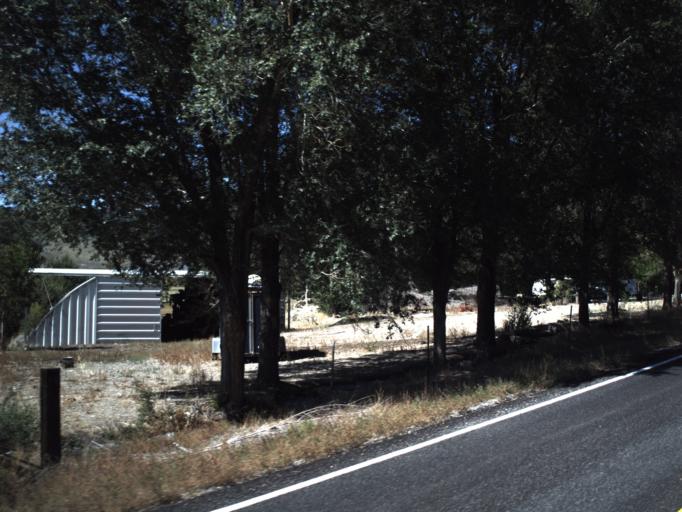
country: US
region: Utah
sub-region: Piute County
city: Junction
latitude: 38.1115
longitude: -111.9897
